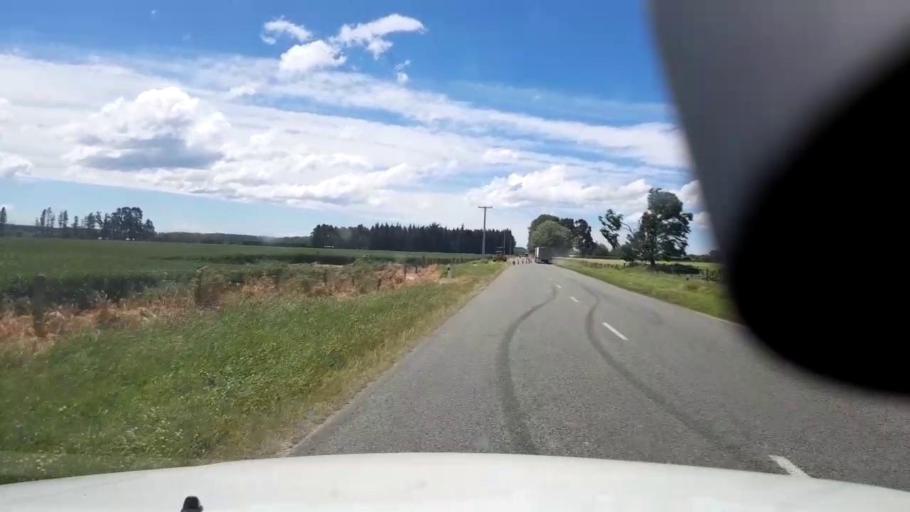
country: NZ
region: Canterbury
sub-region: Timaru District
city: Pleasant Point
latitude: -44.2801
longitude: 171.2462
